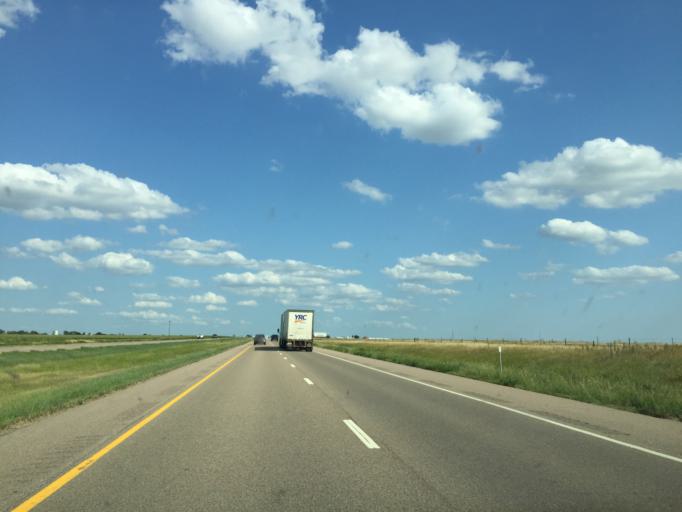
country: US
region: Kansas
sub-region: Gove County
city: Gove
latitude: 39.0680
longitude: -100.2633
